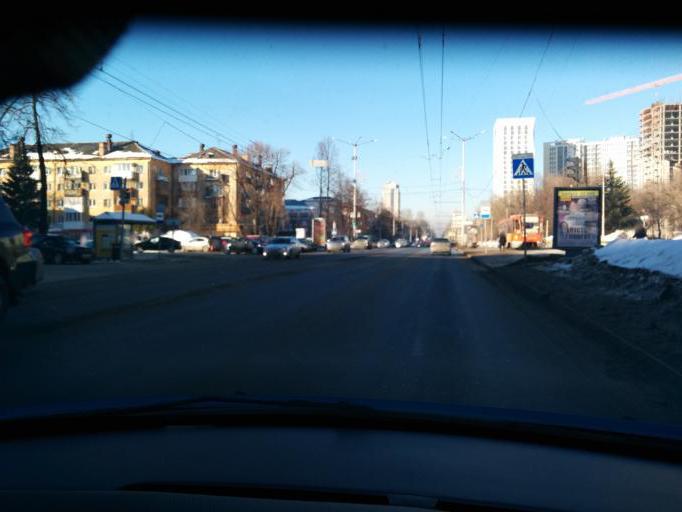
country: RU
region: Perm
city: Perm
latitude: 58.0018
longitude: 56.2575
